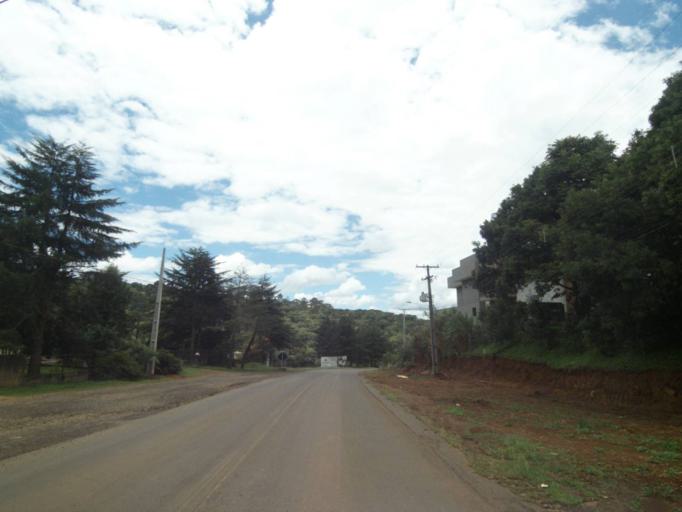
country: BR
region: Parana
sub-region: Pinhao
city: Pinhao
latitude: -26.1570
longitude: -51.5670
